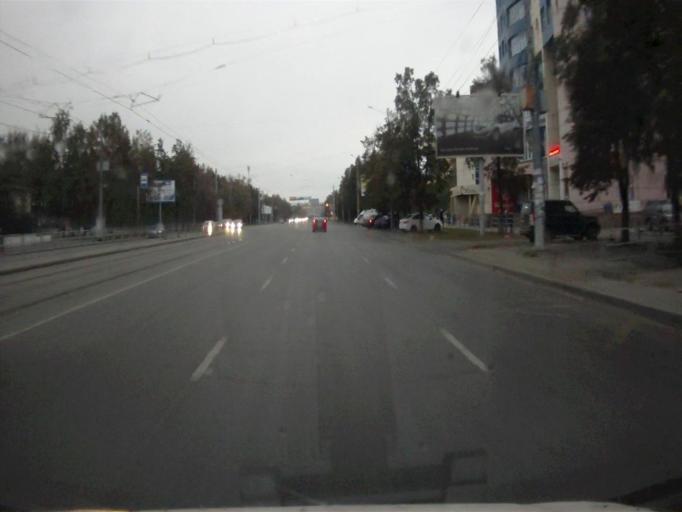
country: RU
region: Chelyabinsk
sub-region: Gorod Chelyabinsk
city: Chelyabinsk
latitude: 55.1739
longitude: 61.3999
